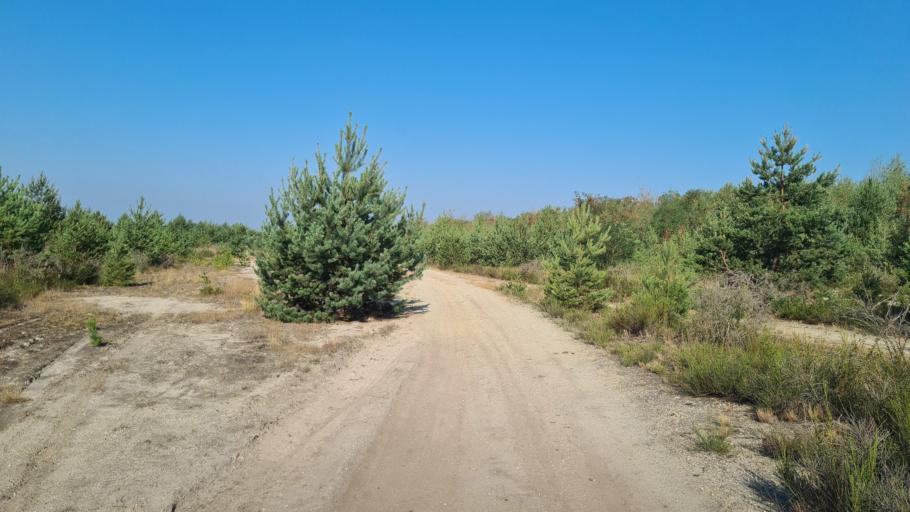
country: DE
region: Brandenburg
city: Sallgast
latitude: 51.5654
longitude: 13.8321
